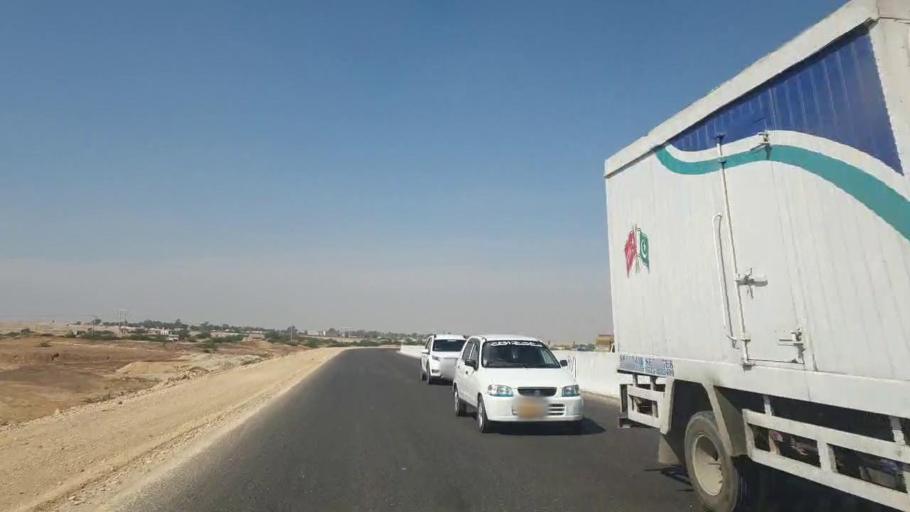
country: PK
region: Sindh
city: Matiari
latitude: 25.6591
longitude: 68.2976
